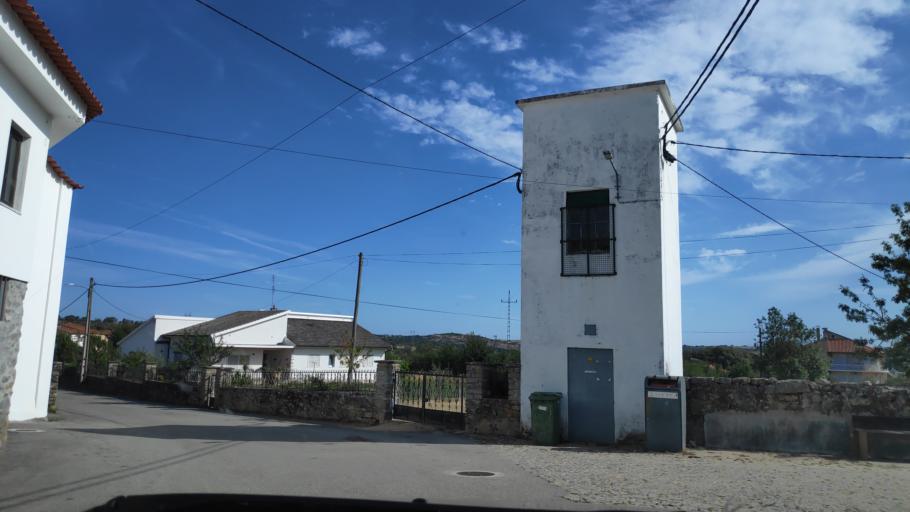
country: ES
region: Castille and Leon
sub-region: Provincia de Zamora
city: Fariza
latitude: 41.4279
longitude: -6.3442
